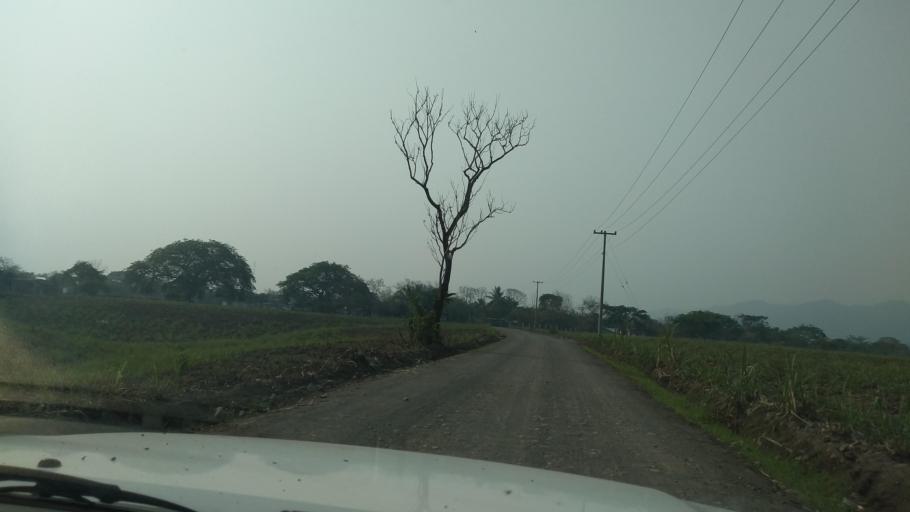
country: MX
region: Veracruz
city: Tezonapa
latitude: 18.6256
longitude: -96.6088
